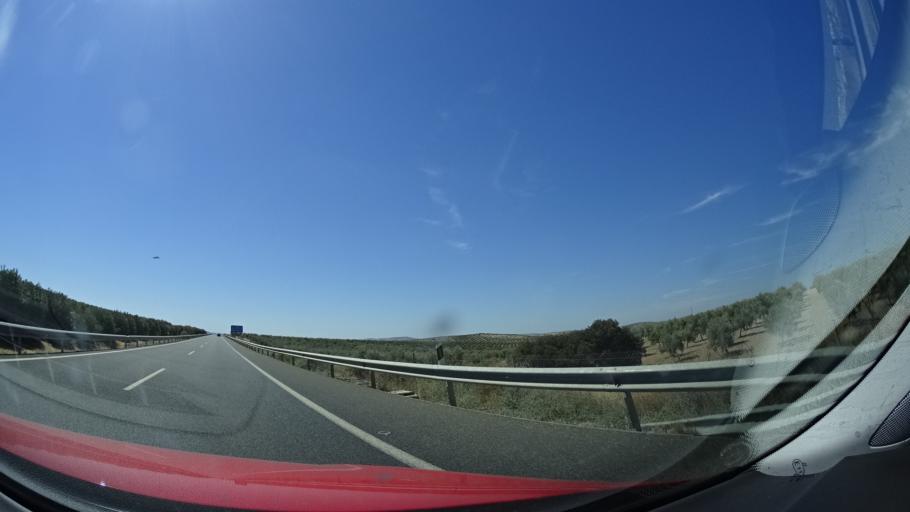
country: ES
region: Andalusia
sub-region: Provincia de Sevilla
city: Gilena
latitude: 37.2710
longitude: -4.9491
